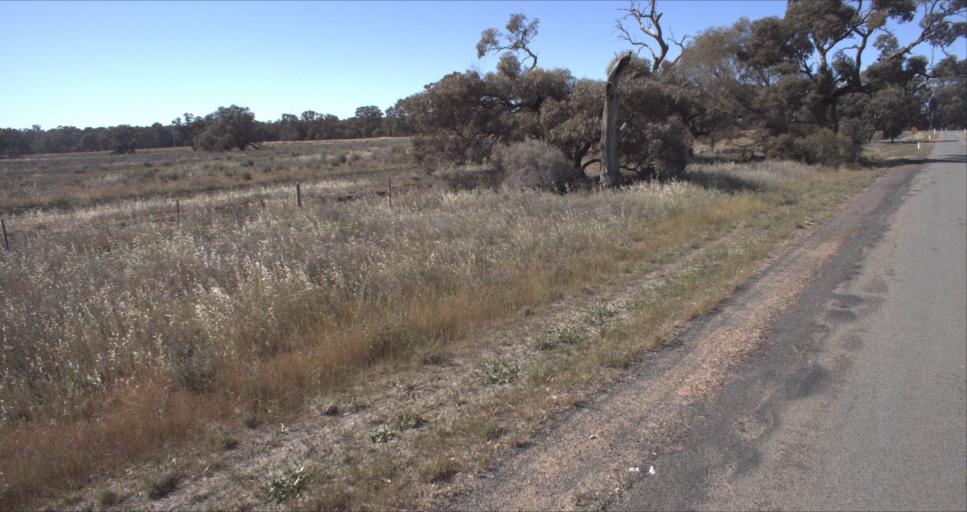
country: AU
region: New South Wales
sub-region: Leeton
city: Leeton
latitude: -34.6030
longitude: 146.2573
